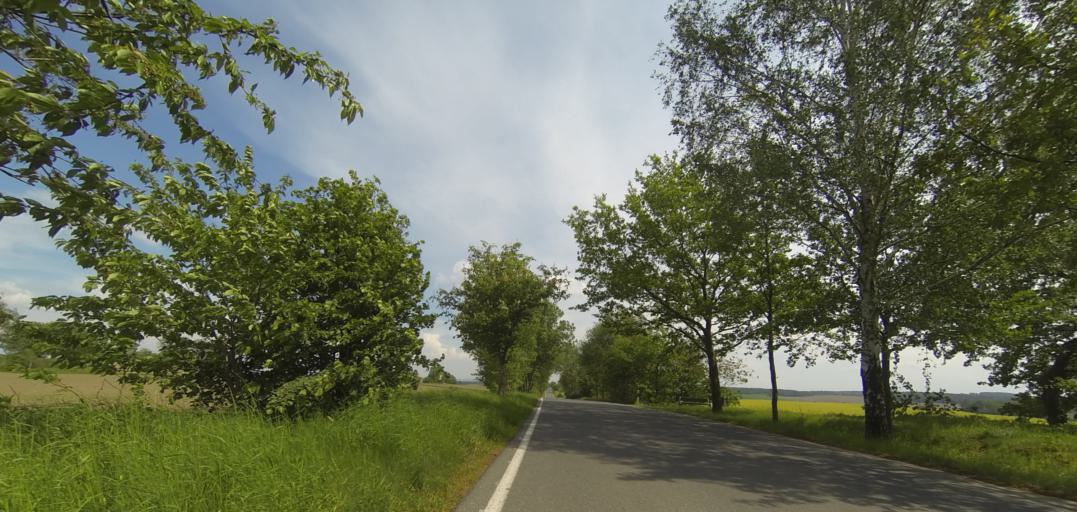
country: DE
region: Saxony
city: Radeberg
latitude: 51.0819
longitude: 13.9144
